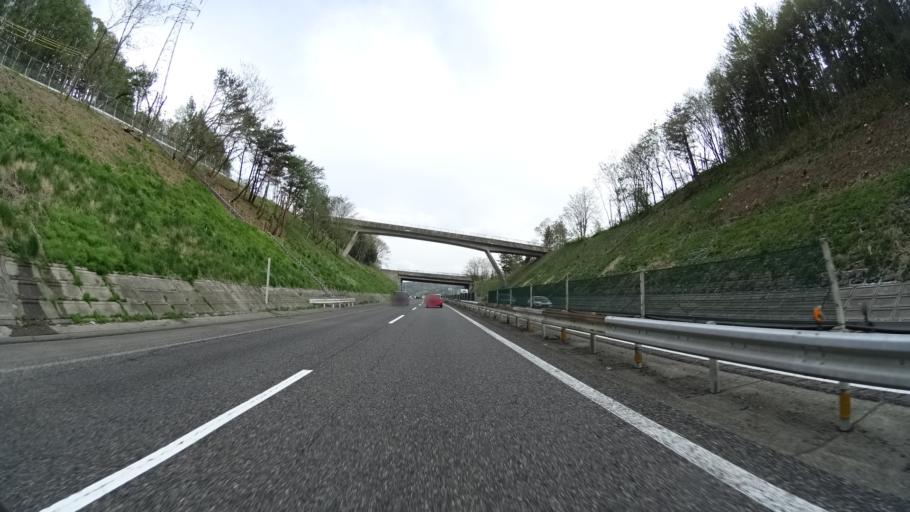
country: JP
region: Nagano
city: Shiojiri
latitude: 36.1048
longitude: 137.9906
